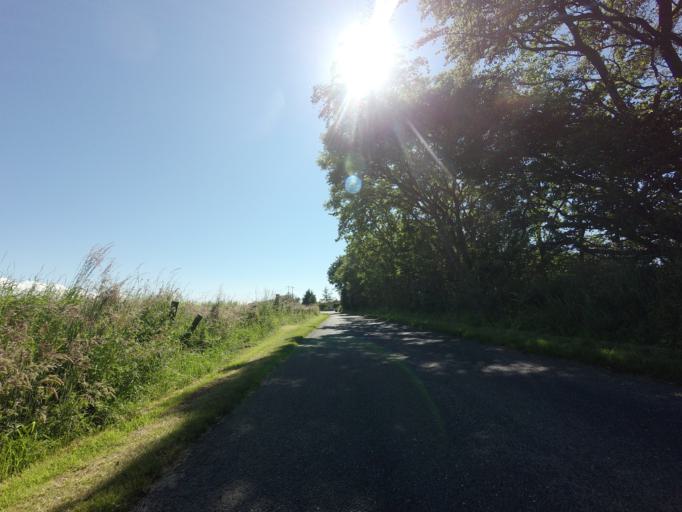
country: GB
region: Scotland
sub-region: Aberdeenshire
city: Macduff
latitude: 57.6591
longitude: -2.4969
